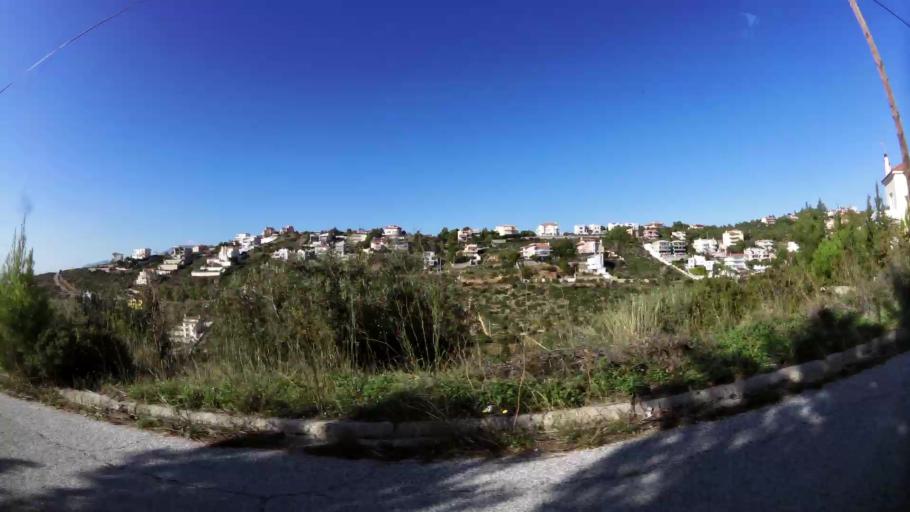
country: GR
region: Attica
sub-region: Nomarchia Anatolikis Attikis
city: Dhrafi
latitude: 38.0262
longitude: 23.8994
